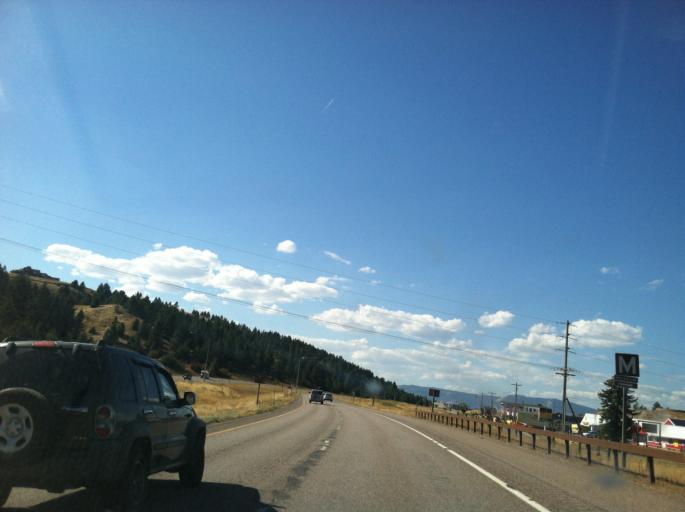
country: US
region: Montana
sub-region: Lake County
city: Polson
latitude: 47.6787
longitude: -114.1122
